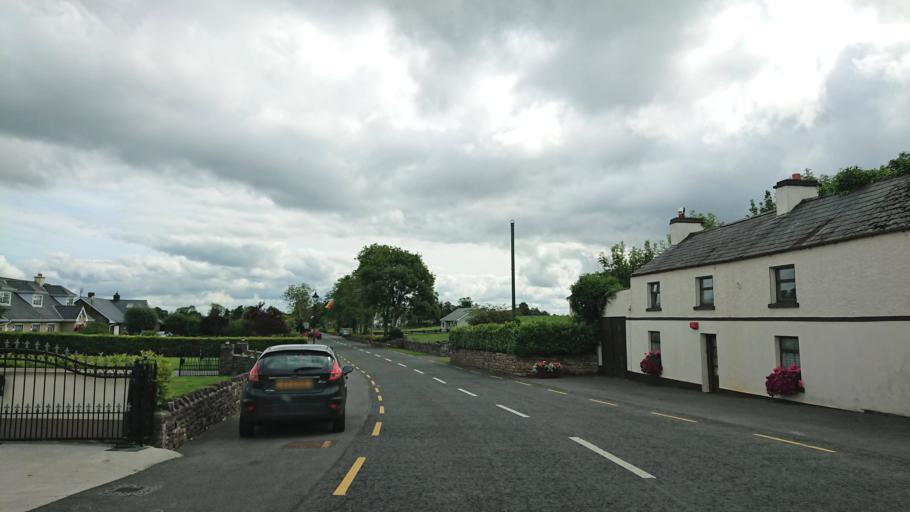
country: IE
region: Connaught
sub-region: County Leitrim
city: Carrick-on-Shannon
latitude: 54.0507
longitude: -8.1366
